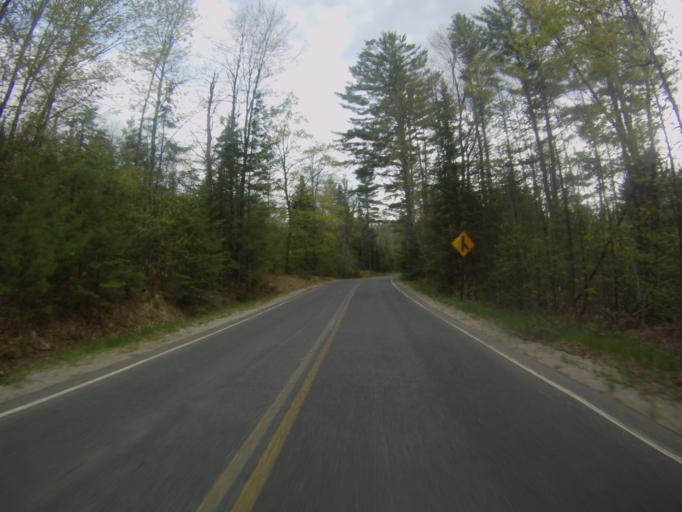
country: US
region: New York
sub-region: Warren County
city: Warrensburg
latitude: 43.8191
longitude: -73.9324
